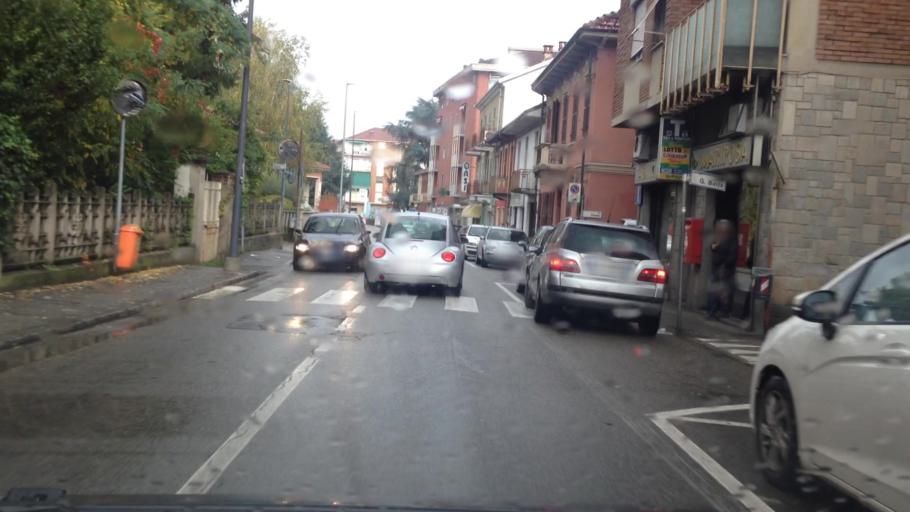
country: IT
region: Piedmont
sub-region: Provincia di Asti
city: Asti
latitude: 44.9068
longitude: 8.2157
